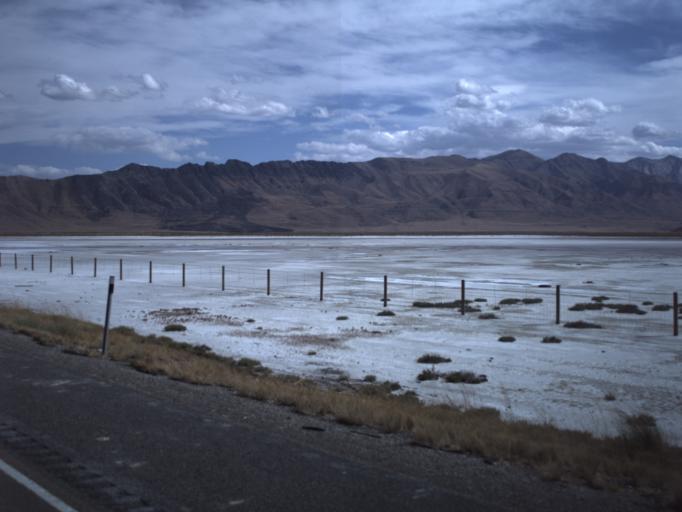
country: US
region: Utah
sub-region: Tooele County
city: Grantsville
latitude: 40.7511
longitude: -112.7075
